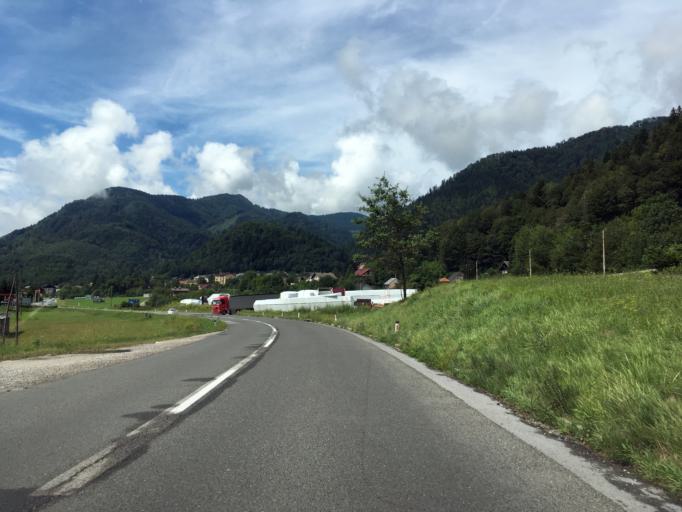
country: SI
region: Jesenice
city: Slovenski Javornik
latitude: 46.4212
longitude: 14.1059
